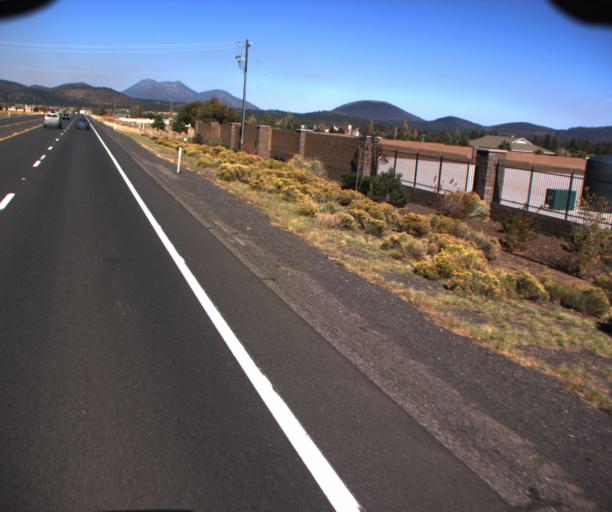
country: US
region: Arizona
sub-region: Coconino County
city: Flagstaff
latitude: 35.2917
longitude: -111.5424
